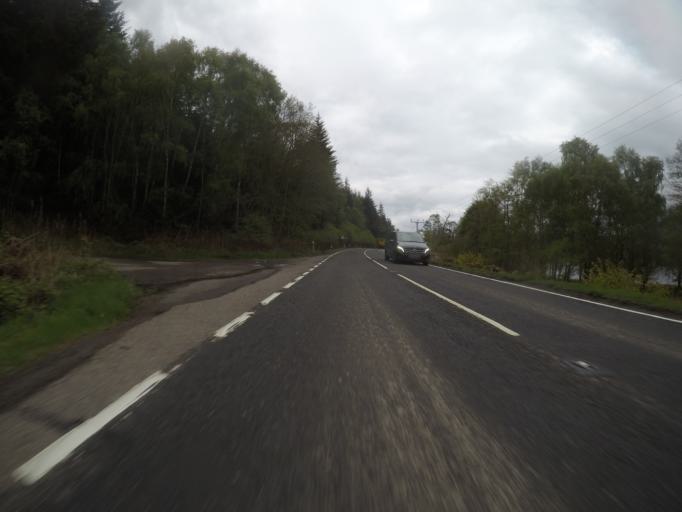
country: GB
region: Scotland
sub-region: Highland
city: Beauly
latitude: 57.2229
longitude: -4.5767
